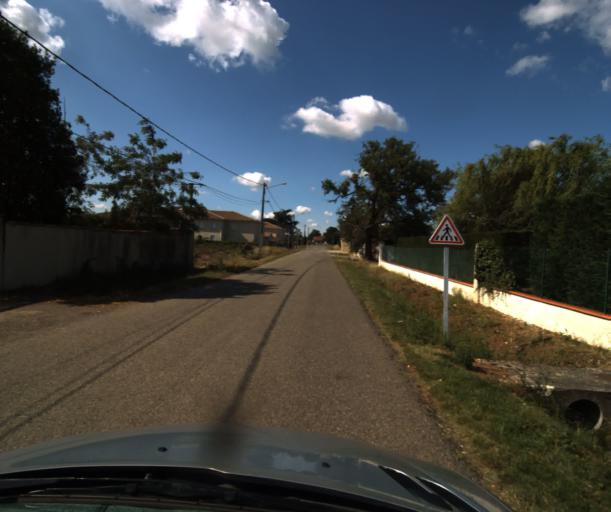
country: FR
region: Midi-Pyrenees
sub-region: Departement du Tarn-et-Garonne
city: Finhan
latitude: 43.9141
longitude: 1.2744
